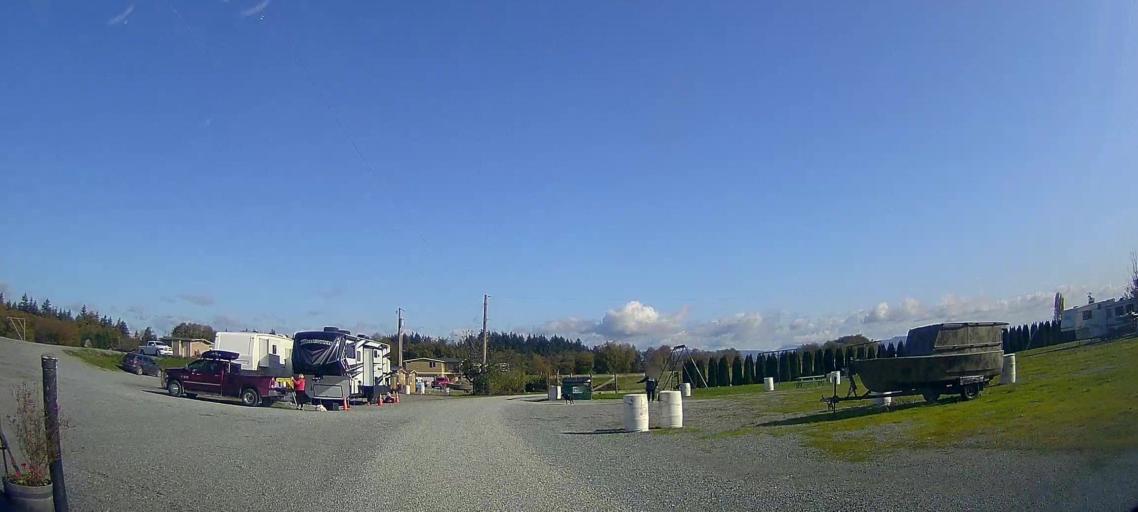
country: US
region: Washington
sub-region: Skagit County
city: Mount Vernon
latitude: 48.3599
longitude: -122.4500
